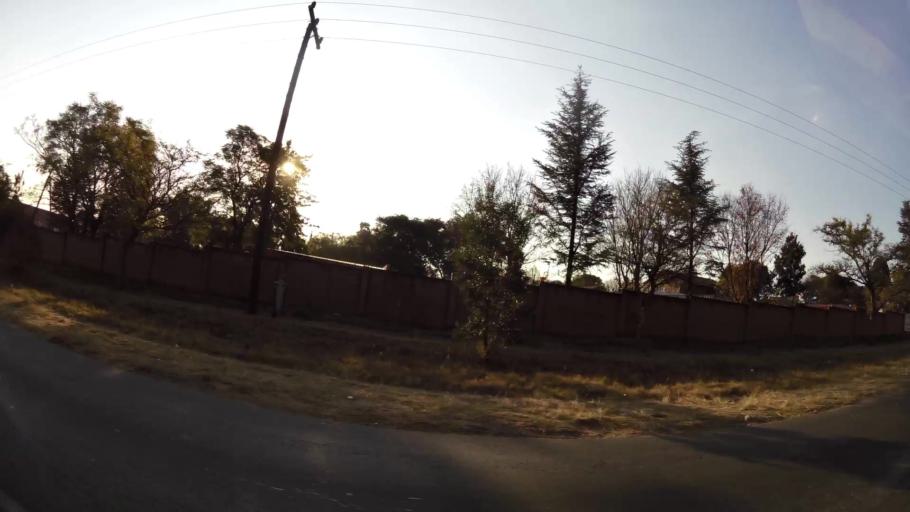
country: ZA
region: Gauteng
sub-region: City of Johannesburg Metropolitan Municipality
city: Midrand
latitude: -26.0271
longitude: 28.1466
